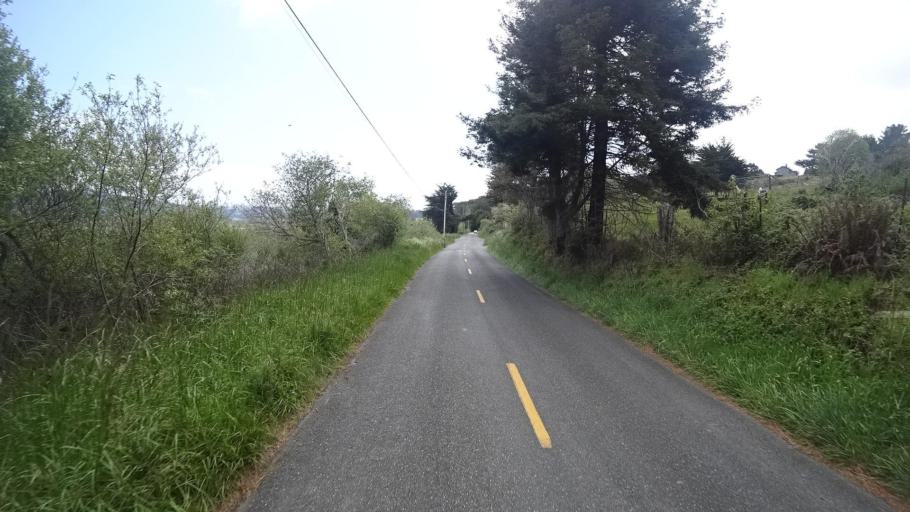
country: US
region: California
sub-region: Humboldt County
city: Humboldt Hill
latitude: 40.6860
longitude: -124.2330
